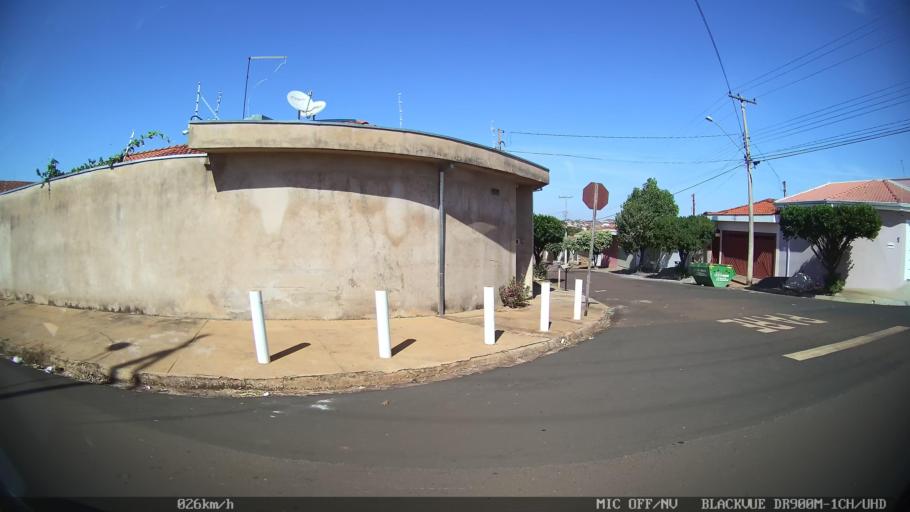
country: BR
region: Sao Paulo
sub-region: Batatais
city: Batatais
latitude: -20.8890
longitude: -47.5723
